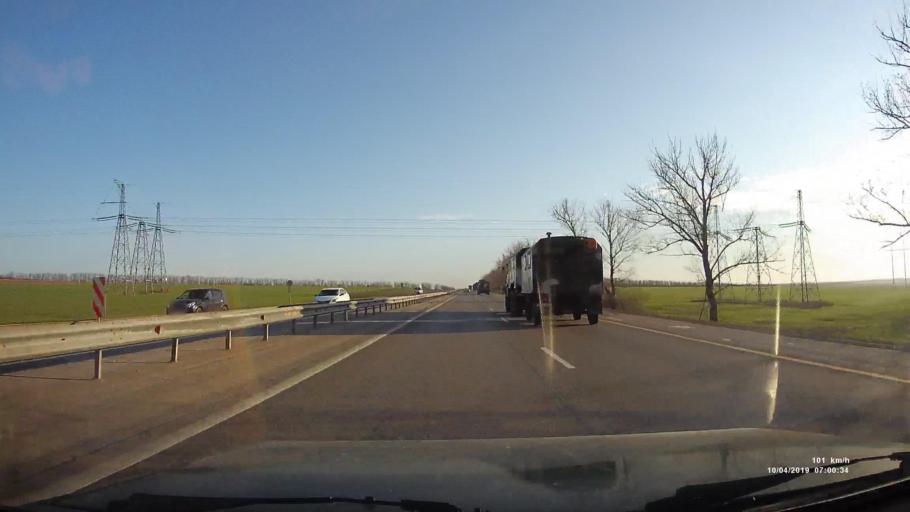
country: RU
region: Rostov
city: Krasyukovskaya
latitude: 47.5830
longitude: 39.9750
